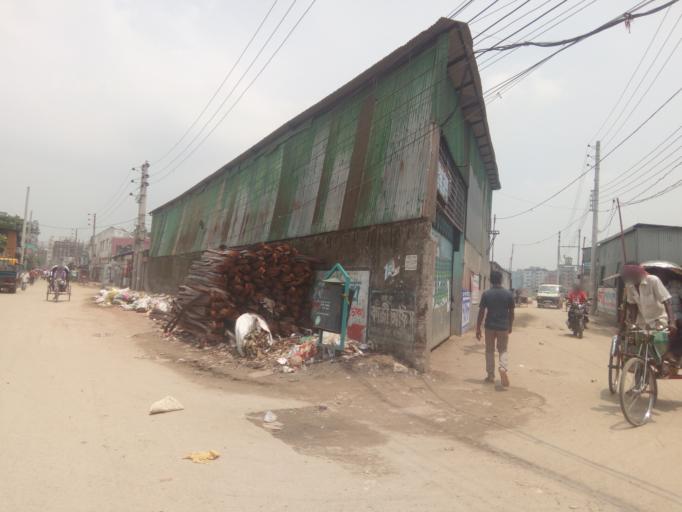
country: BD
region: Dhaka
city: Paltan
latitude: 23.7550
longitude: 90.4277
